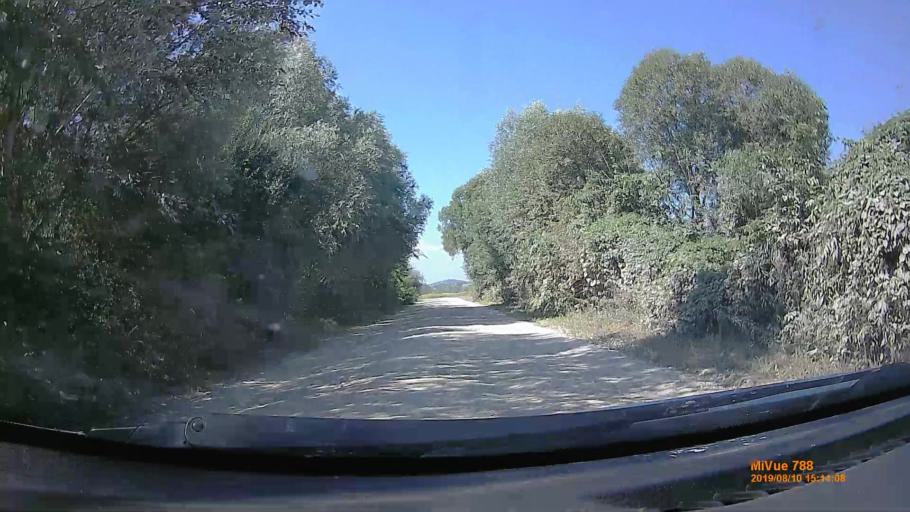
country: HU
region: Somogy
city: Fonyod
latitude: 46.6955
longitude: 17.5591
